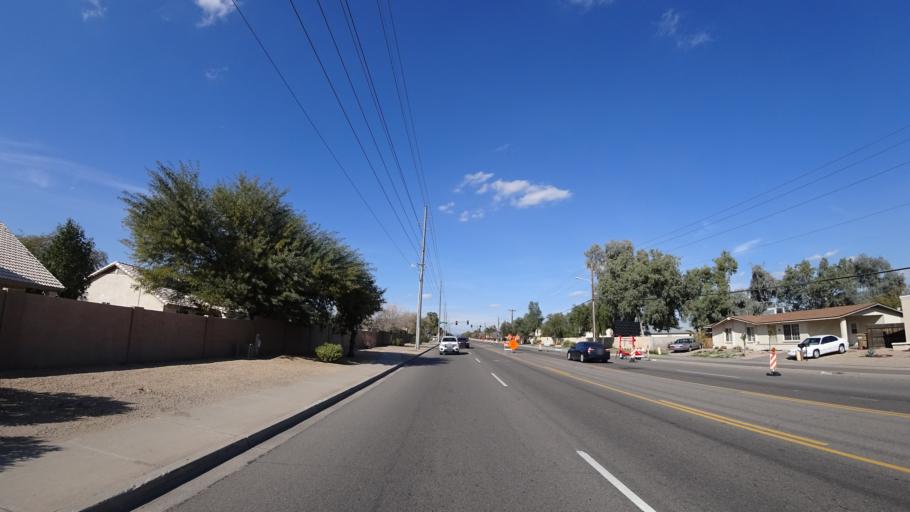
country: US
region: Arizona
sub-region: Maricopa County
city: Peoria
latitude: 33.5875
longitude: -112.2204
